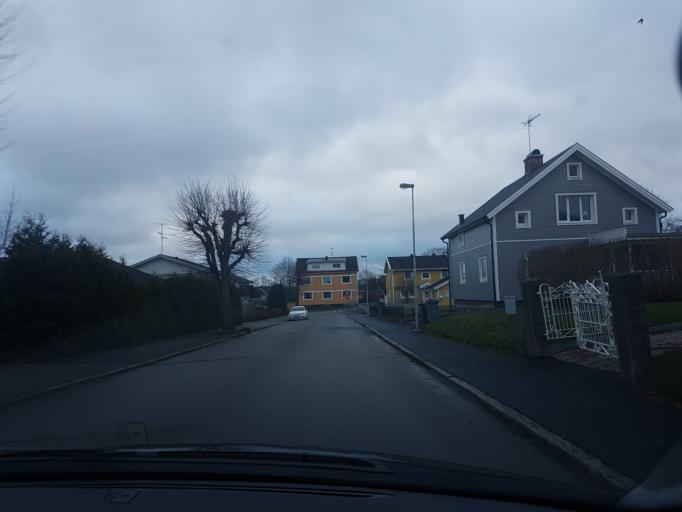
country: SE
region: Joenkoeping
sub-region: Vetlanda Kommun
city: Vetlanda
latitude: 57.4277
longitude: 15.0761
